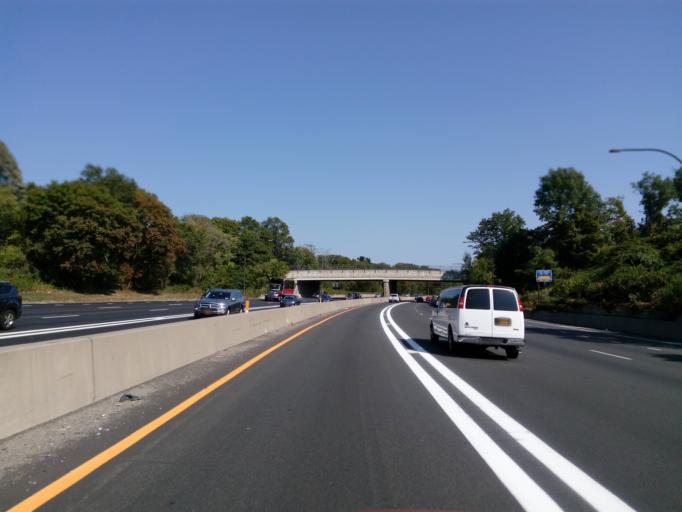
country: US
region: New York
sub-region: Nassau County
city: East Hills
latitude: 40.7836
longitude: -73.6168
